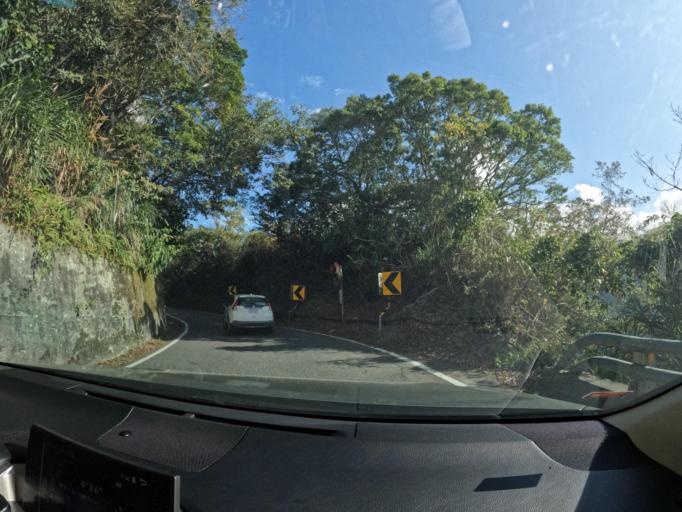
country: TW
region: Taiwan
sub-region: Taitung
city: Taitung
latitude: 23.1922
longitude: 121.0213
